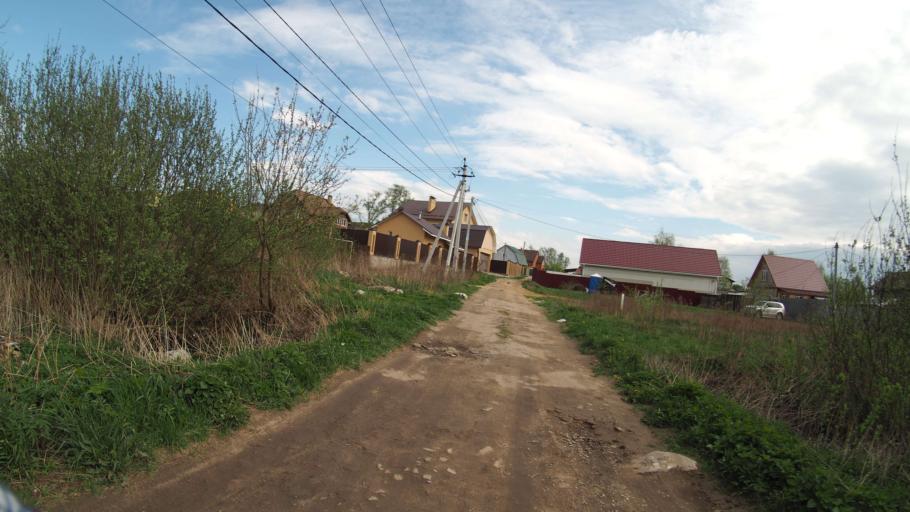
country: RU
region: Moskovskaya
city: Ramenskoye
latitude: 55.5481
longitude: 38.2398
